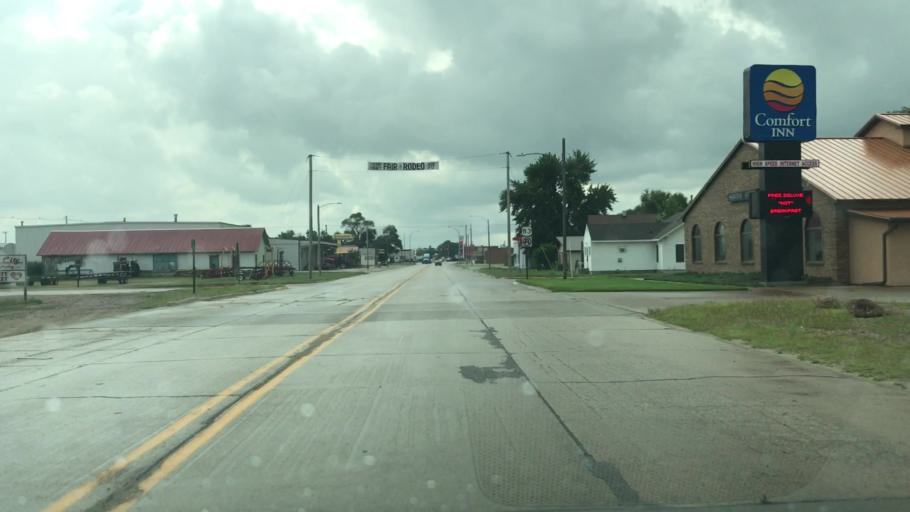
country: US
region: Nebraska
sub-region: Cherry County
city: Valentine
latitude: 42.8714
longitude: -100.5506
